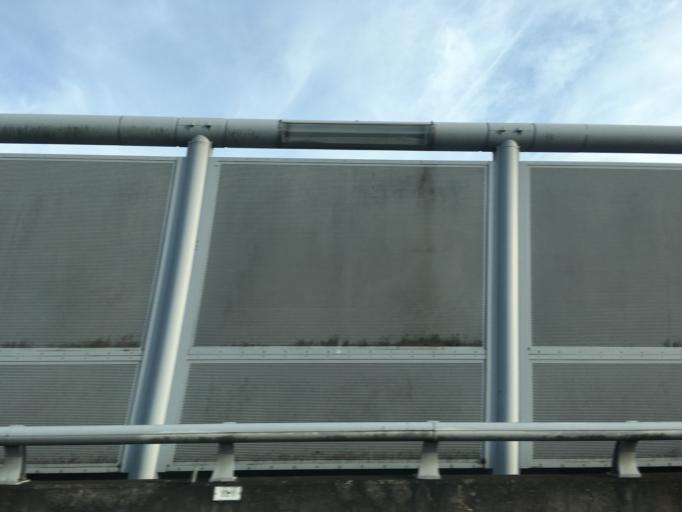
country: FR
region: Ile-de-France
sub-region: Departement des Yvelines
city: Montesson
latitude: 48.9174
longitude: 2.1167
